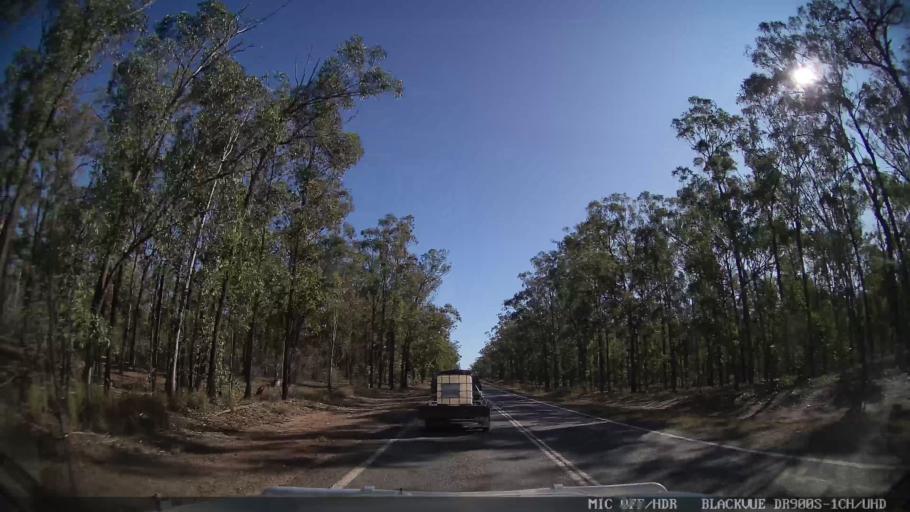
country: AU
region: Queensland
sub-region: Bundaberg
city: Childers
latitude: -25.2166
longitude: 152.0726
